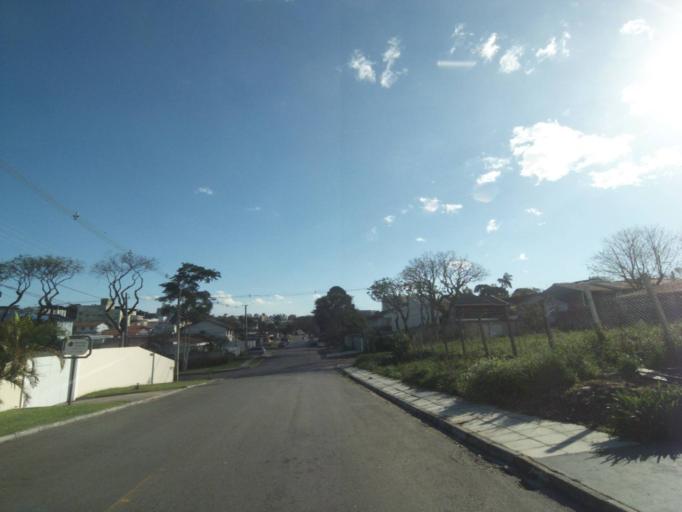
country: BR
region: Parana
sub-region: Curitiba
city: Curitiba
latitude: -25.3916
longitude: -49.2480
